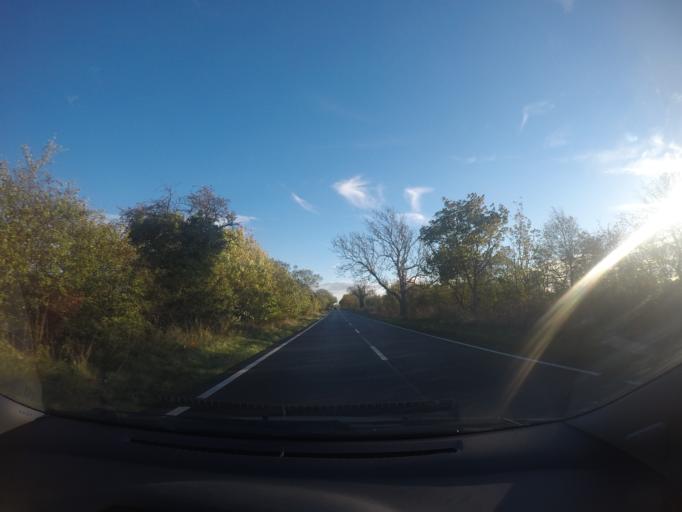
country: GB
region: England
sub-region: City of York
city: York
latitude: 53.9844
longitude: -1.0838
